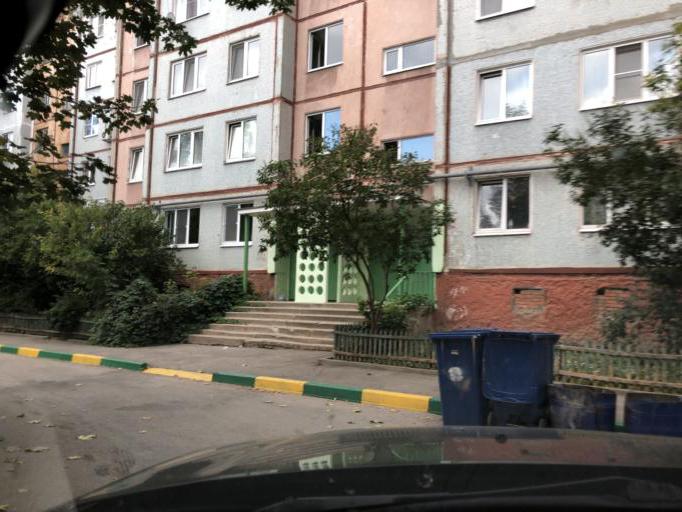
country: RU
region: Tula
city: Tula
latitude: 54.2106
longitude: 37.6050
